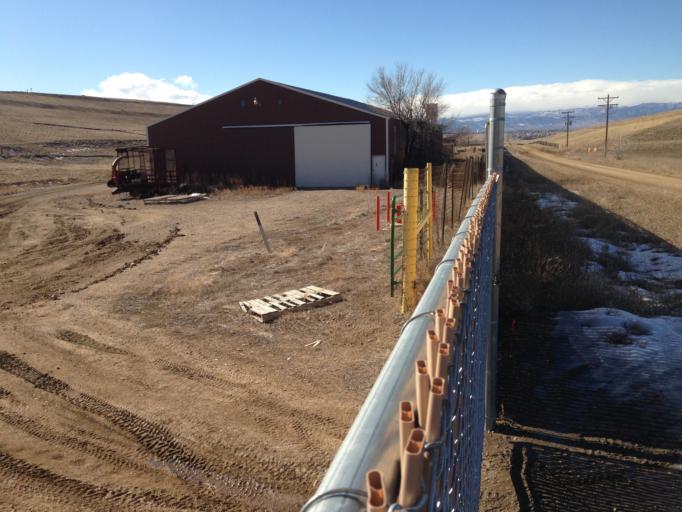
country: US
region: Colorado
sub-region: Boulder County
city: Erie
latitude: 40.0292
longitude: -105.0256
